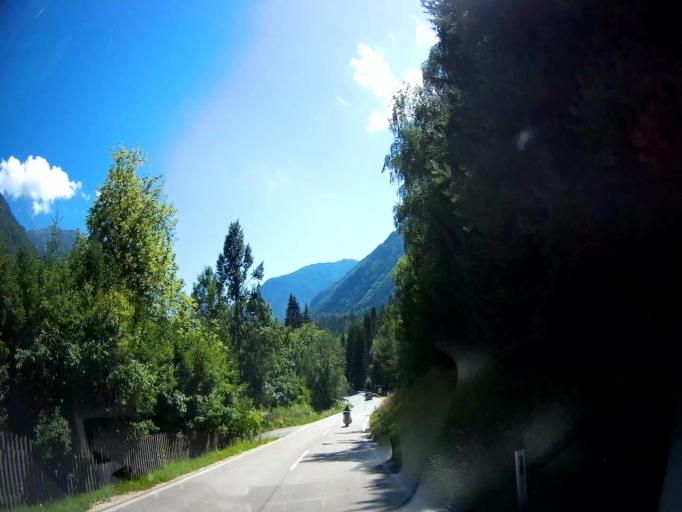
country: AT
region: Carinthia
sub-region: Politischer Bezirk Volkermarkt
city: Gallizien
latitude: 46.5363
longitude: 14.4588
